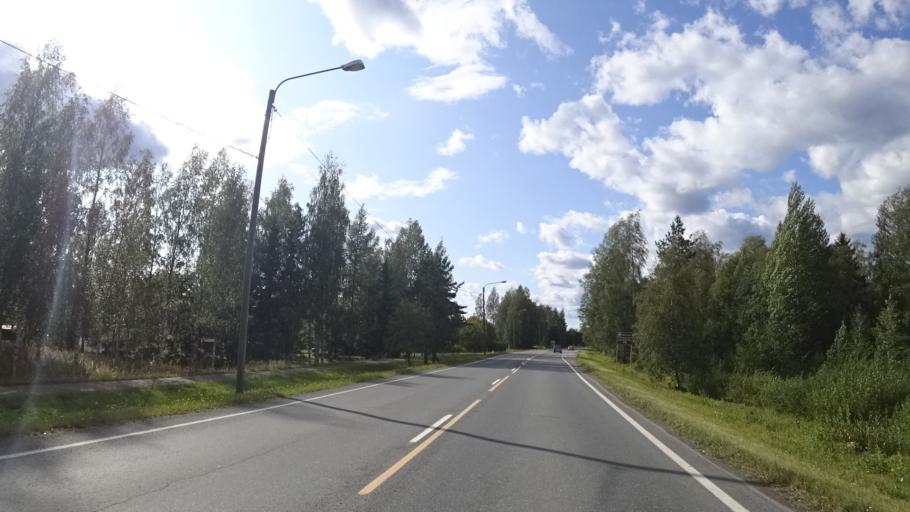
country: FI
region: North Karelia
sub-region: Keski-Karjala
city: Tohmajaervi
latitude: 62.2231
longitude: 30.3437
